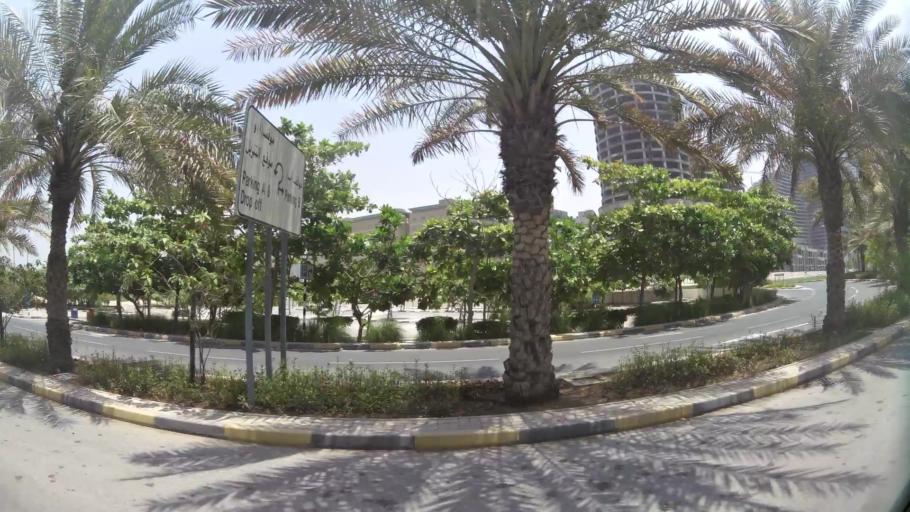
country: AE
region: Ash Shariqah
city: Sharjah
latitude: 25.3314
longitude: 55.3598
